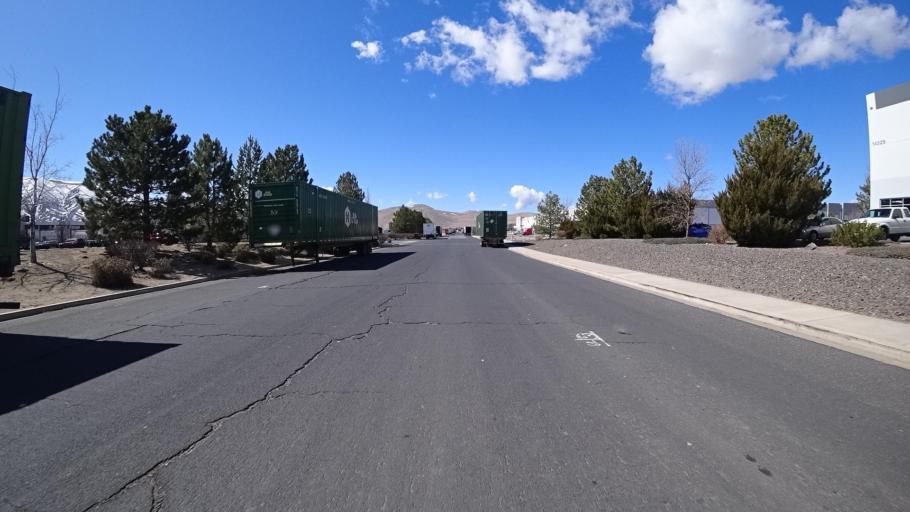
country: US
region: Nevada
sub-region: Washoe County
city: Lemmon Valley
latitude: 39.6546
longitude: -119.8889
